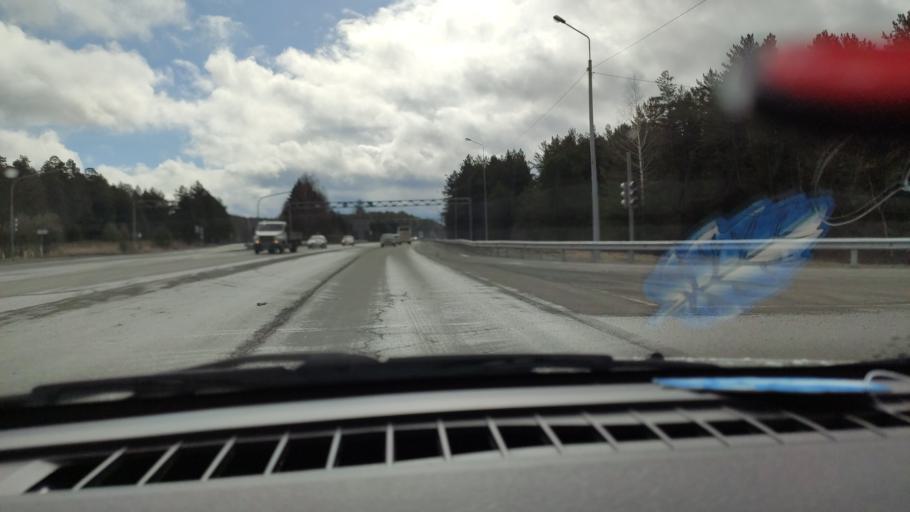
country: RU
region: Sverdlovsk
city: Talitsa
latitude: 56.8732
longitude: 60.0349
